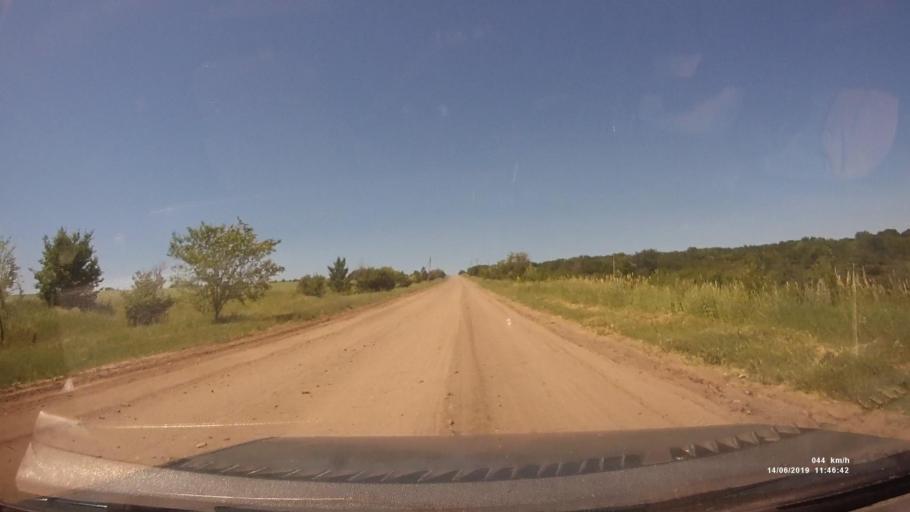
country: RU
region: Rostov
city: Kazanskaya
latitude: 49.8510
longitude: 41.3023
